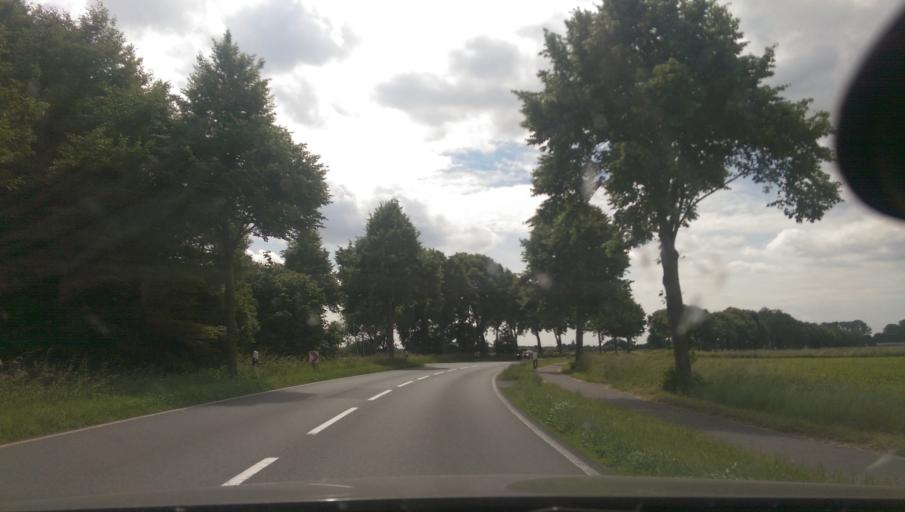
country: DE
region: Lower Saxony
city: Oyten
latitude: 53.0928
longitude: 9.0588
